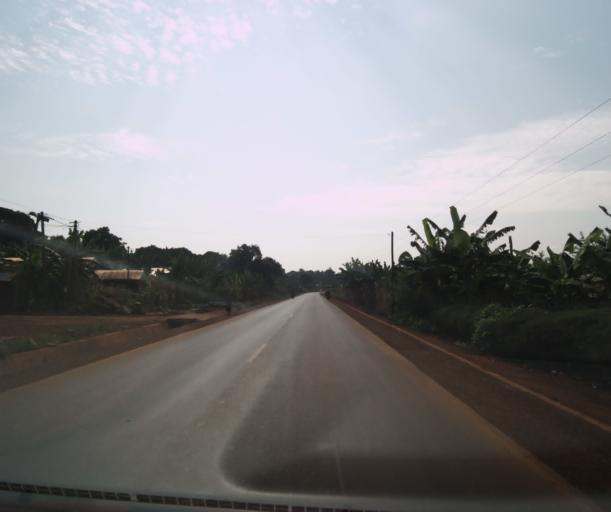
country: CM
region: West
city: Mbouda
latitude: 5.6193
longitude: 10.2767
